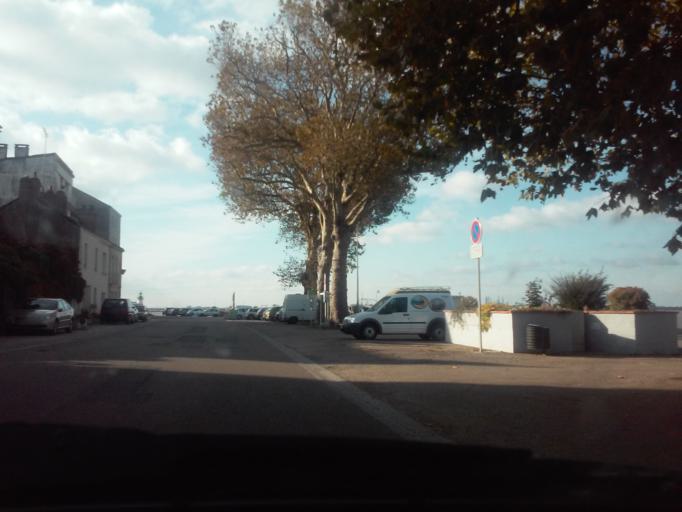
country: FR
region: Pays de la Loire
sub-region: Departement de la Loire-Atlantique
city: Saint-Paimboeuf
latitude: 47.2895
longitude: -2.0287
